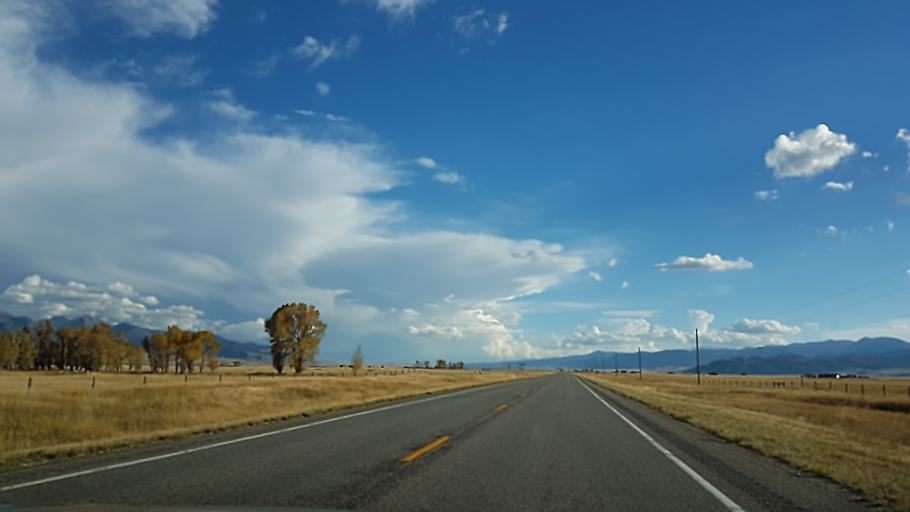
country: US
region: Montana
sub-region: Madison County
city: Virginia City
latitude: 45.1955
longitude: -111.6788
